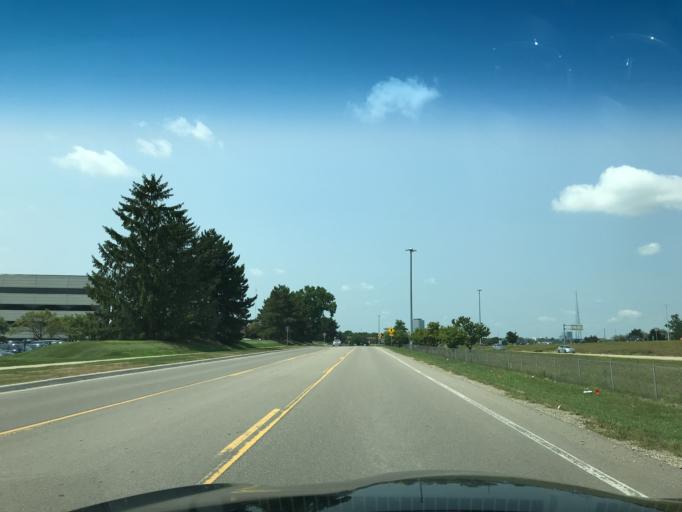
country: US
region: Michigan
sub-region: Oakland County
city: Bingham Farms
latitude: 42.4844
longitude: -83.2702
